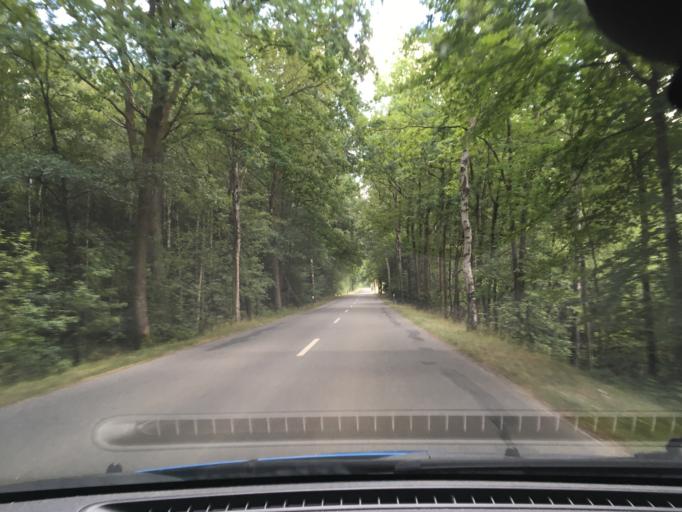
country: DE
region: Lower Saxony
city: Wriedel
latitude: 53.0470
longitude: 10.2591
